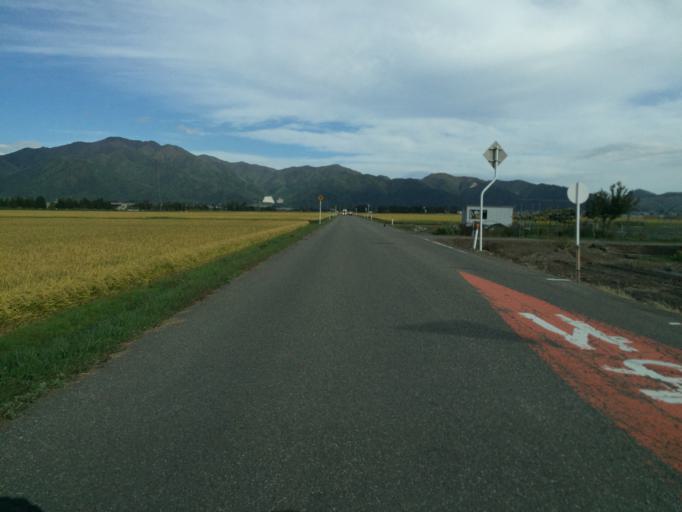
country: JP
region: Fukushima
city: Inawashiro
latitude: 37.5442
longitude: 140.0901
